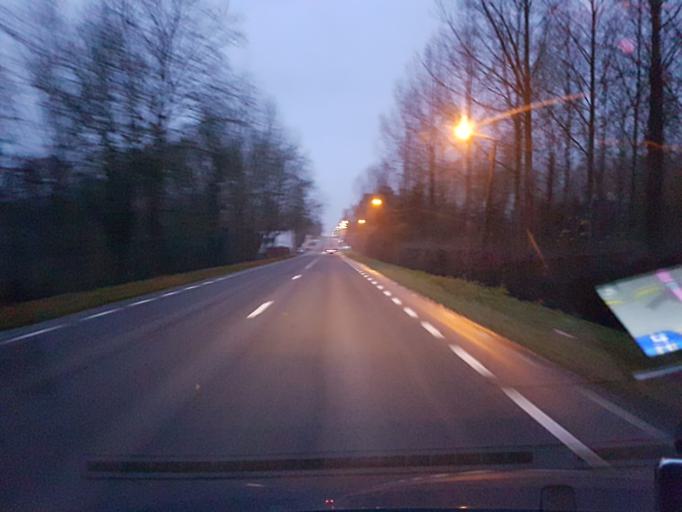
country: BE
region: Wallonia
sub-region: Province de Namur
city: Eghezee
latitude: 50.6065
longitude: 4.8962
